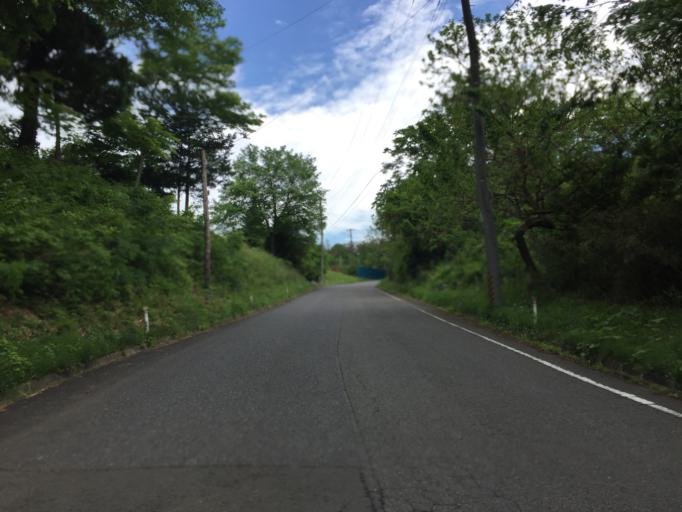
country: JP
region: Fukushima
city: Nihommatsu
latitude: 37.6367
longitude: 140.5027
